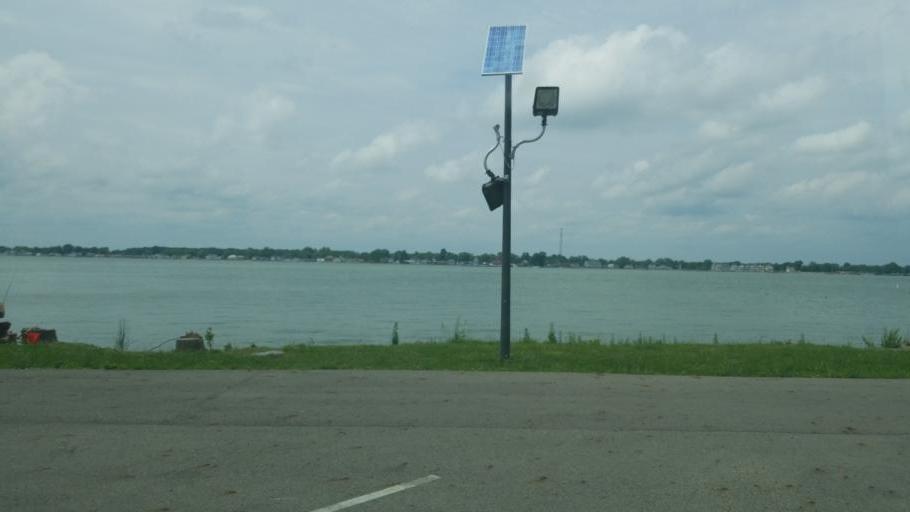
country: US
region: Ohio
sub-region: Fairfield County
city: Fairfield Beach
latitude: 39.9205
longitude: -82.4769
